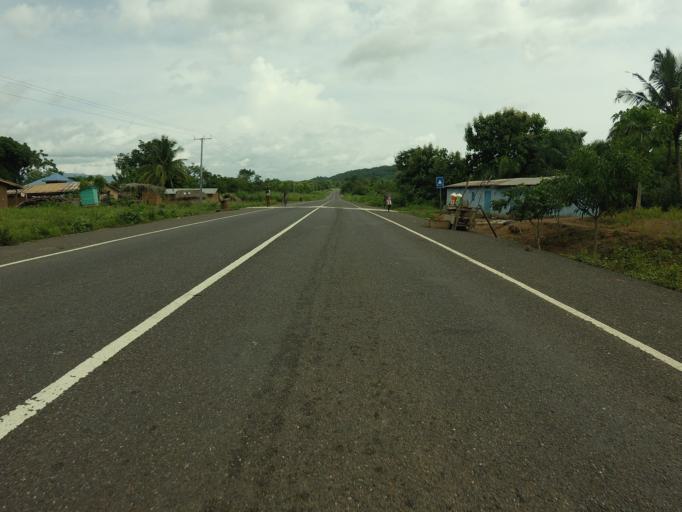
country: TG
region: Plateaux
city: Badou
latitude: 7.9522
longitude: 0.5545
